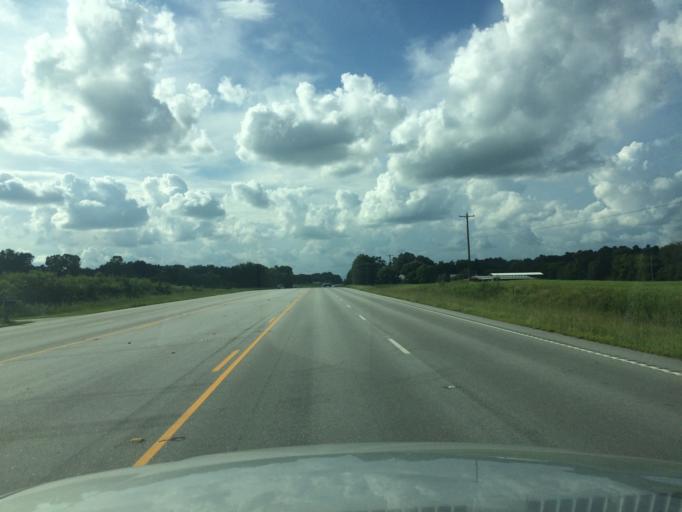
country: US
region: South Carolina
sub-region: Greenville County
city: Five Forks
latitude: 34.8049
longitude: -82.1265
